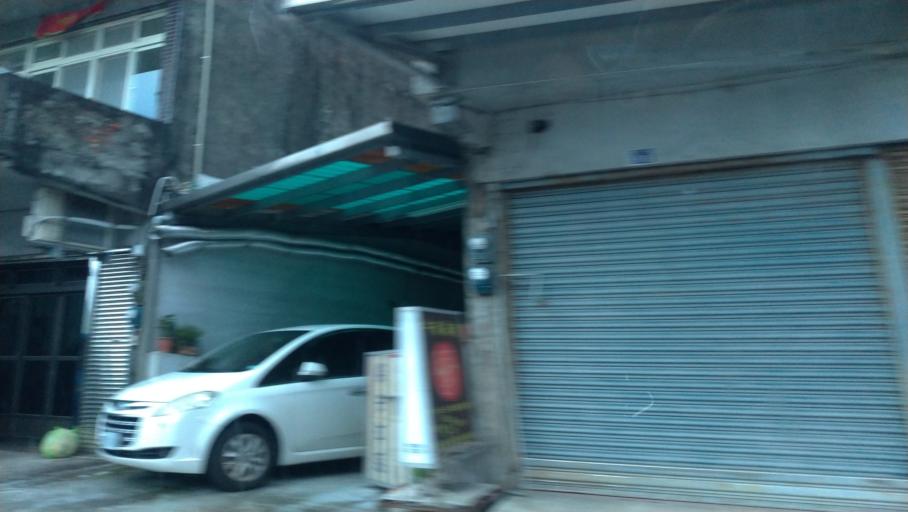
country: TW
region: Taiwan
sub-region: Yilan
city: Yilan
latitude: 24.8450
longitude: 121.8075
